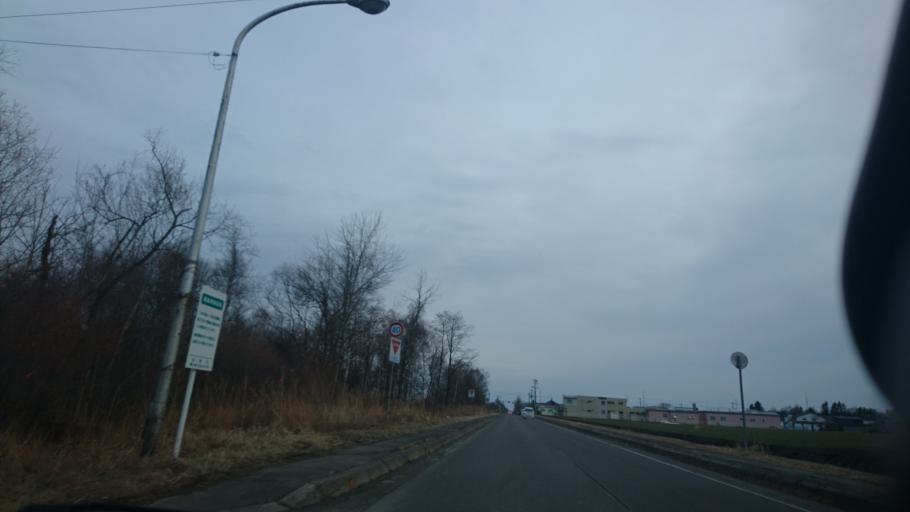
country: JP
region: Hokkaido
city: Otofuke
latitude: 42.9744
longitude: 143.1984
